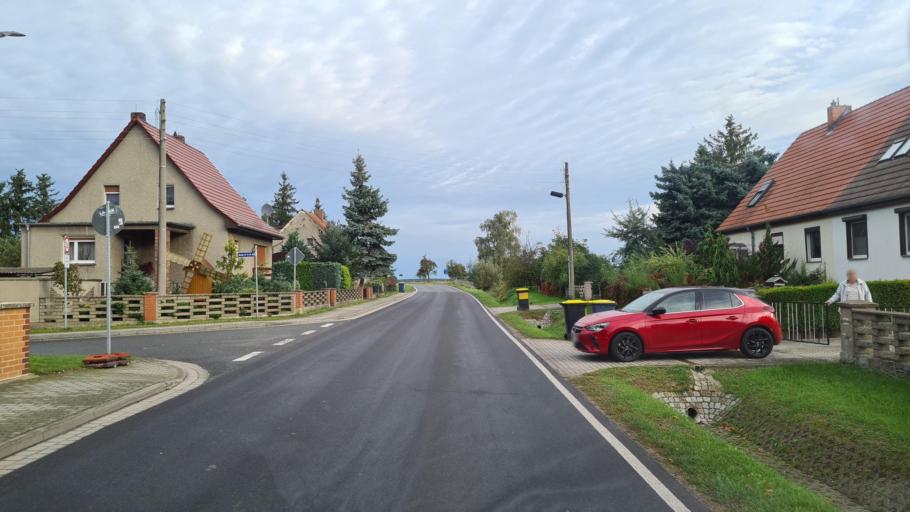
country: DE
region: Brandenburg
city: Luckau
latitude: 51.8723
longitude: 13.7234
